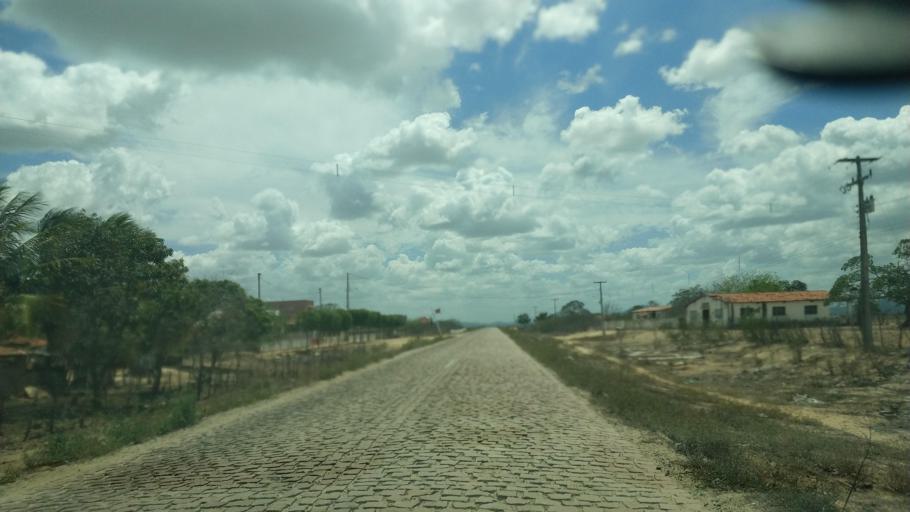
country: BR
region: Rio Grande do Norte
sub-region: Sao Paulo Do Potengi
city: Sao Paulo do Potengi
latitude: -5.9800
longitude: -35.8574
